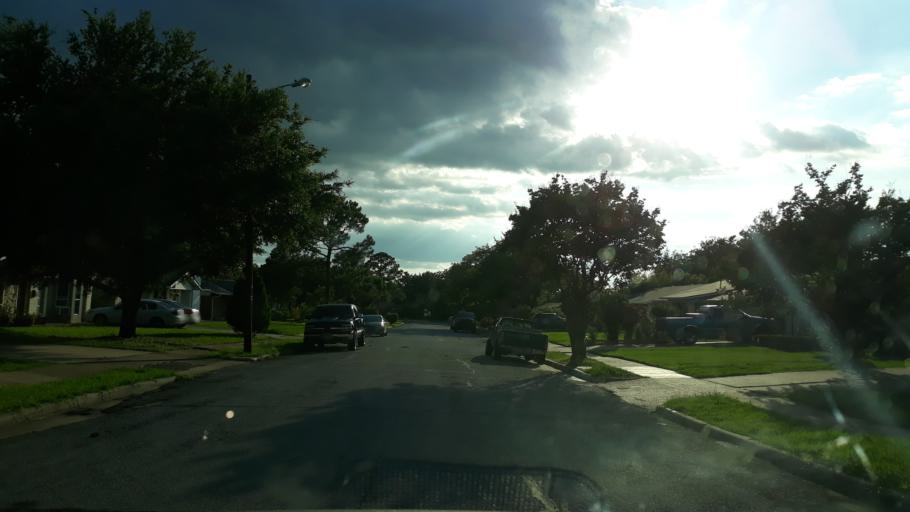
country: US
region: Texas
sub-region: Dallas County
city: Irving
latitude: 32.8520
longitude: -96.9967
